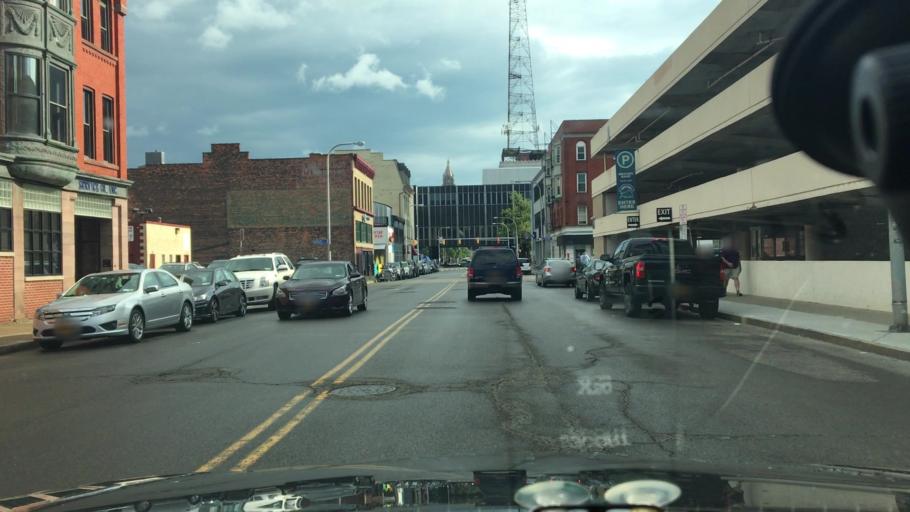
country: US
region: New York
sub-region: Erie County
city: Buffalo
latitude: 42.8874
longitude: -78.8715
